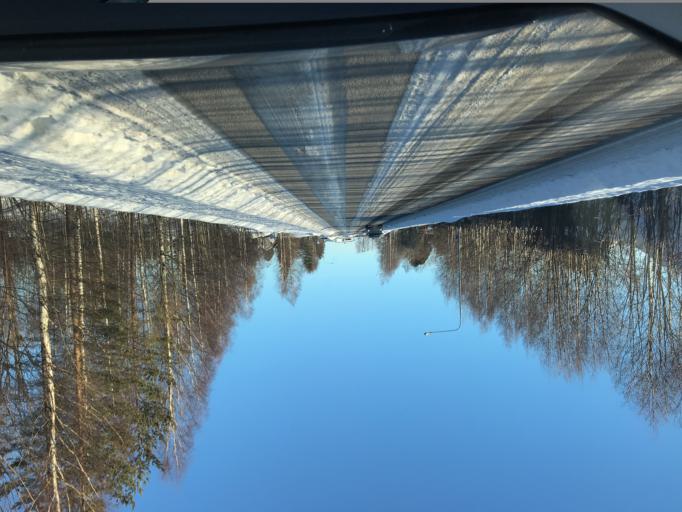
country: SE
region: Norrbotten
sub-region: Lulea Kommun
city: Sodra Sunderbyn
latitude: 65.6607
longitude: 21.9510
